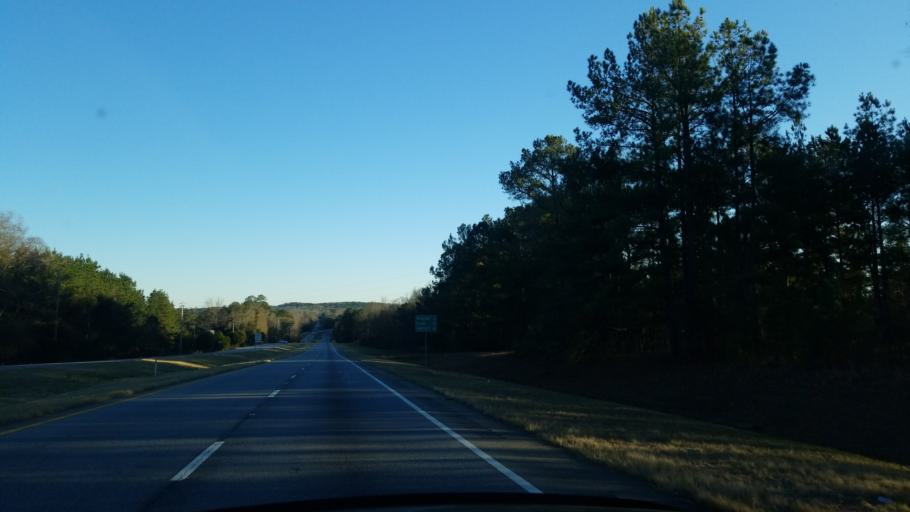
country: US
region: Georgia
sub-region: Chattahoochee County
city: Cusseta
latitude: 32.2893
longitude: -84.7664
